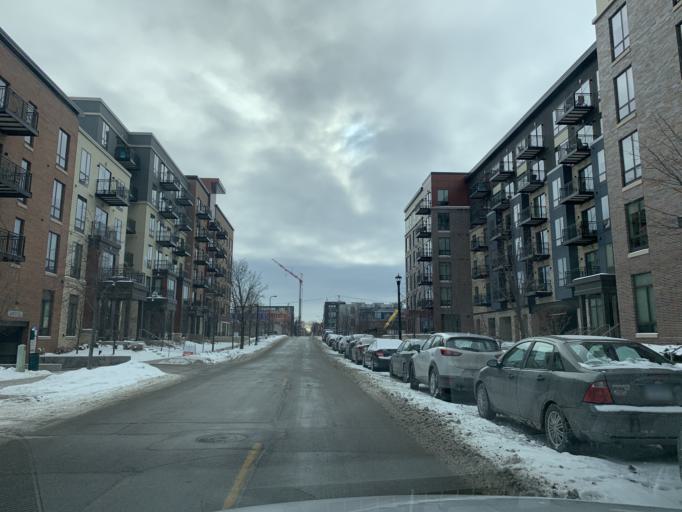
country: US
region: Minnesota
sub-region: Hennepin County
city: Minneapolis
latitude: 44.9515
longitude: -93.2945
